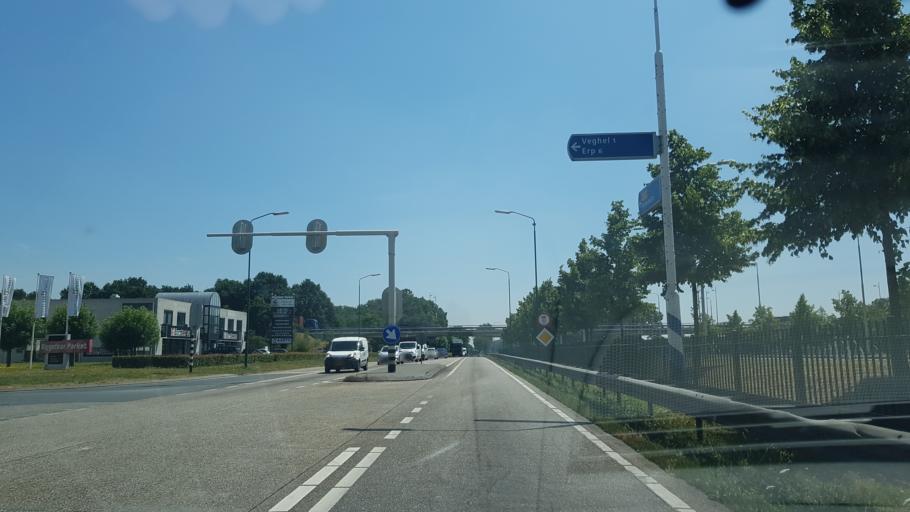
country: NL
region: North Brabant
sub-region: Gemeente Veghel
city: Veghel
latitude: 51.6092
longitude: 5.5309
